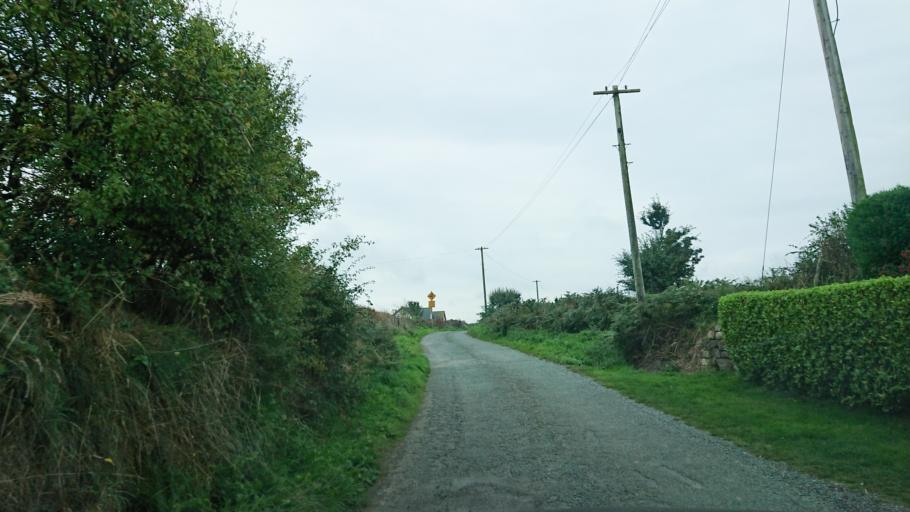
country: IE
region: Munster
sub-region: Waterford
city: Dunmore East
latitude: 52.1688
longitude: -6.9981
